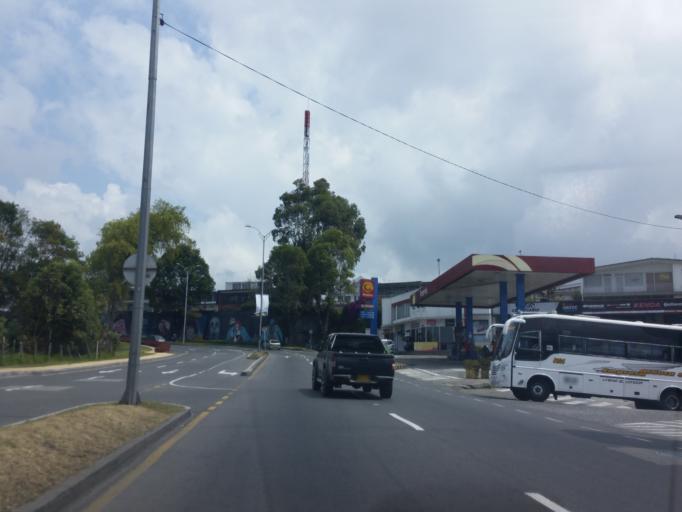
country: CO
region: Caldas
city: Manizales
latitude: 5.0621
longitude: -75.5264
